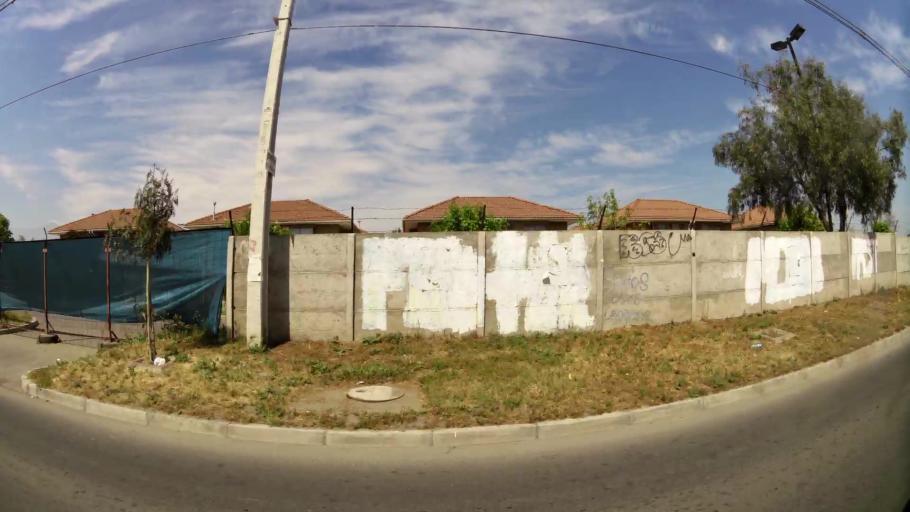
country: CL
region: Santiago Metropolitan
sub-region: Provincia de Cordillera
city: Puente Alto
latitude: -33.6000
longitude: -70.5922
